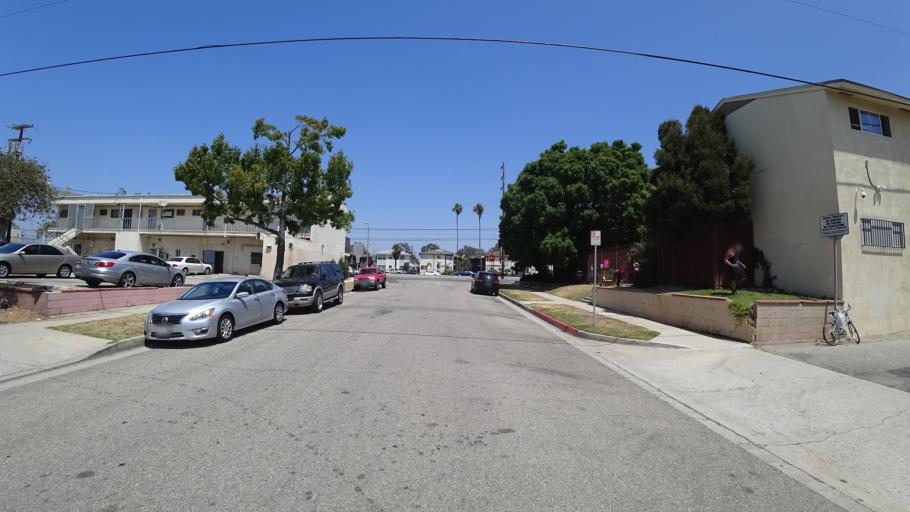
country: US
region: California
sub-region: Los Angeles County
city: West Athens
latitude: 33.9303
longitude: -118.3216
